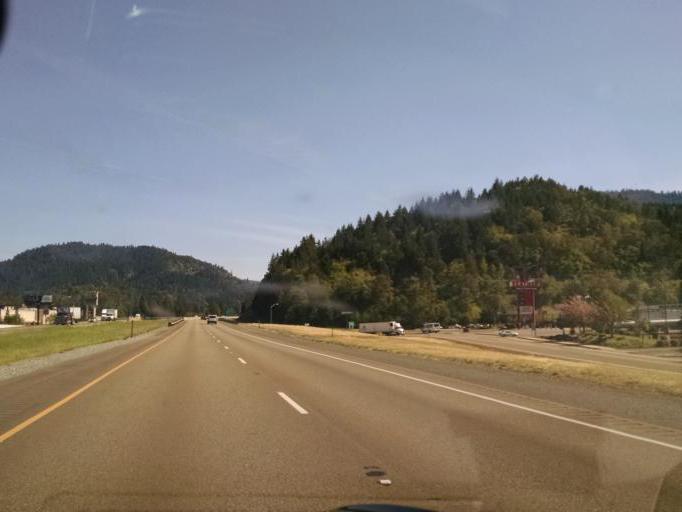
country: US
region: Oregon
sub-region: Douglas County
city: Canyonville
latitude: 42.9428
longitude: -123.2904
